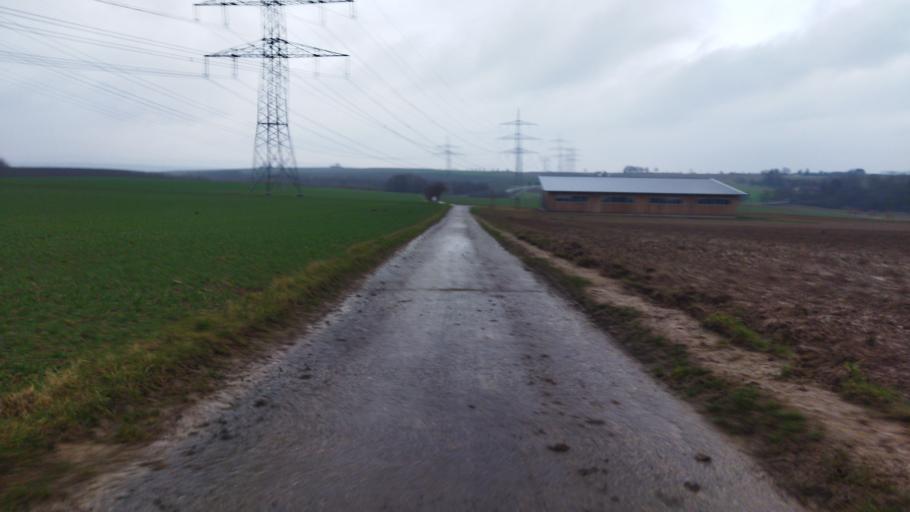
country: DE
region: Baden-Wuerttemberg
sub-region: Regierungsbezirk Stuttgart
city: Neckarwestheim
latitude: 49.0509
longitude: 9.2009
